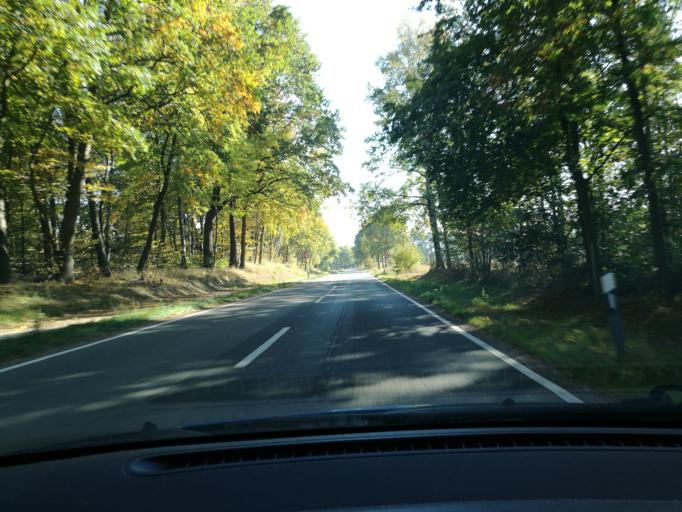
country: DE
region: Lower Saxony
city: Vastorf
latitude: 53.2058
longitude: 10.5331
